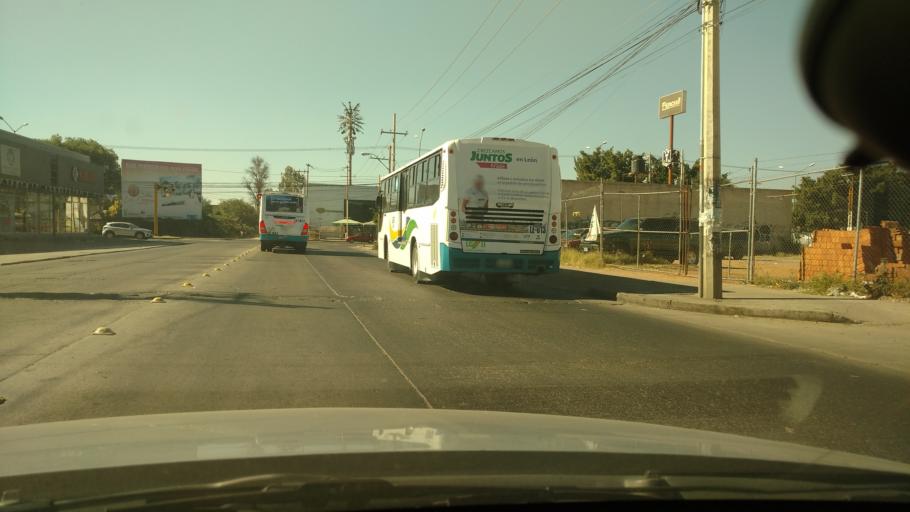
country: MX
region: Guanajuato
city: Leon
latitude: 21.1483
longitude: -101.6743
